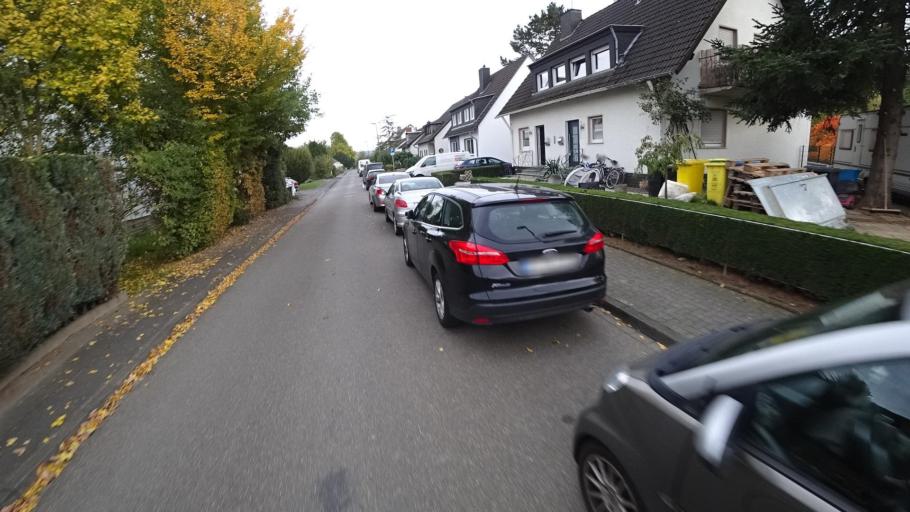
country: DE
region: Rheinland-Pfalz
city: Remagen
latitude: 50.5526
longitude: 7.2188
